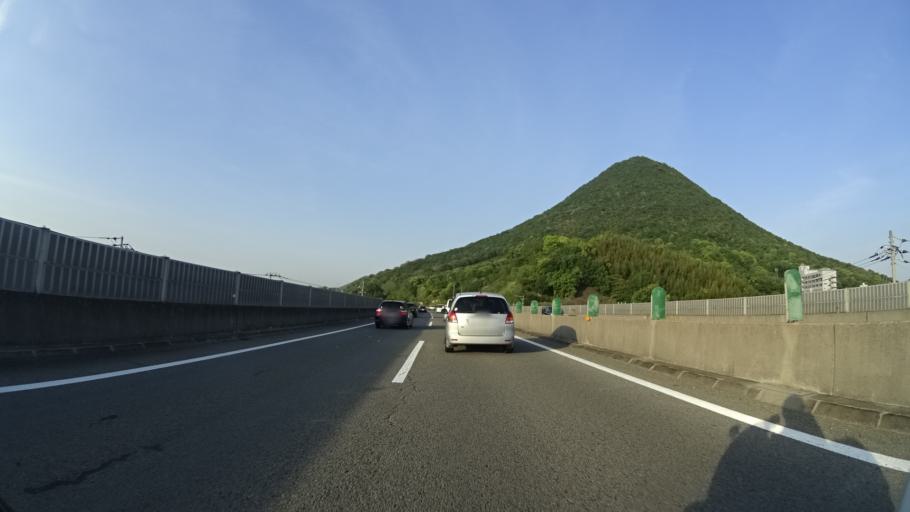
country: JP
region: Kagawa
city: Sakaidecho
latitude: 34.2732
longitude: 133.8332
